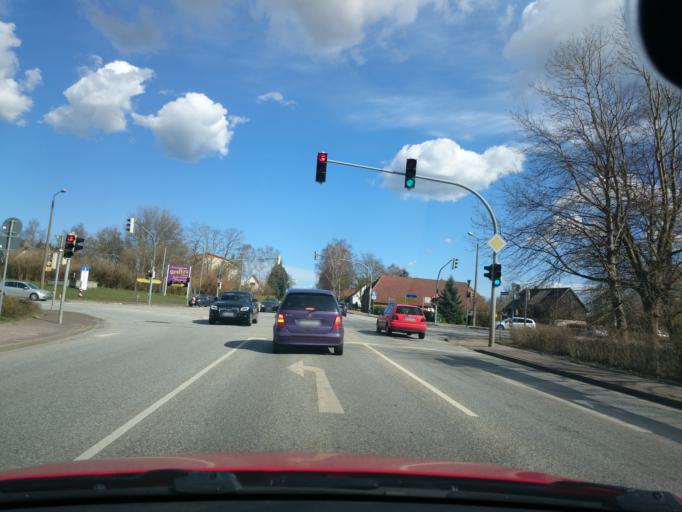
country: DE
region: Mecklenburg-Vorpommern
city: Barth
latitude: 54.2953
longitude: 12.7186
